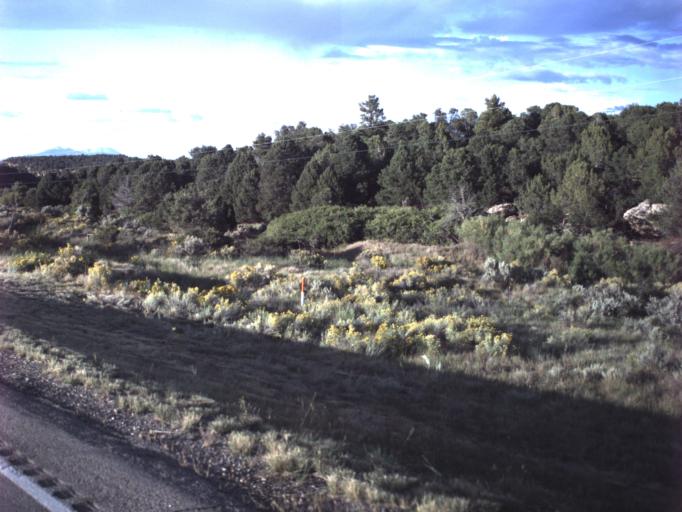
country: US
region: Utah
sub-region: San Juan County
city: Monticello
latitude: 37.9665
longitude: -109.3570
